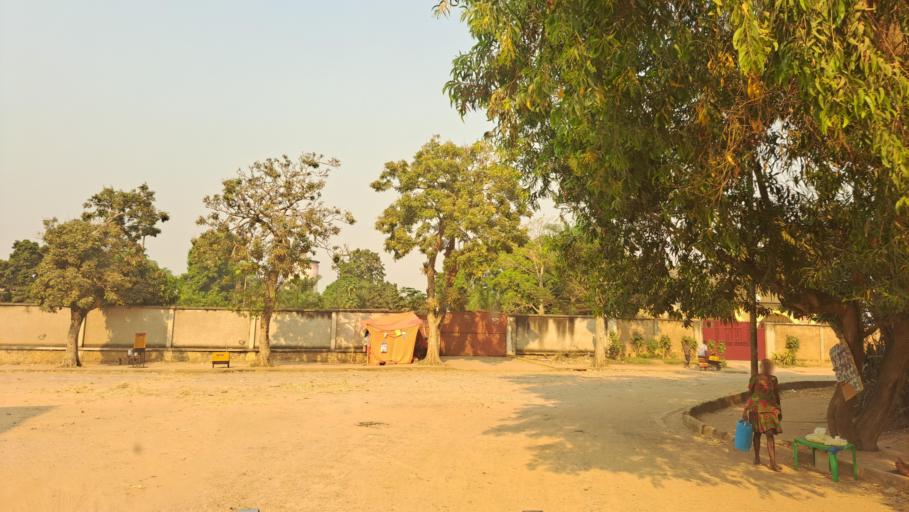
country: CD
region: Kasai-Occidental
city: Kananga
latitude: -5.8927
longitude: 22.4126
